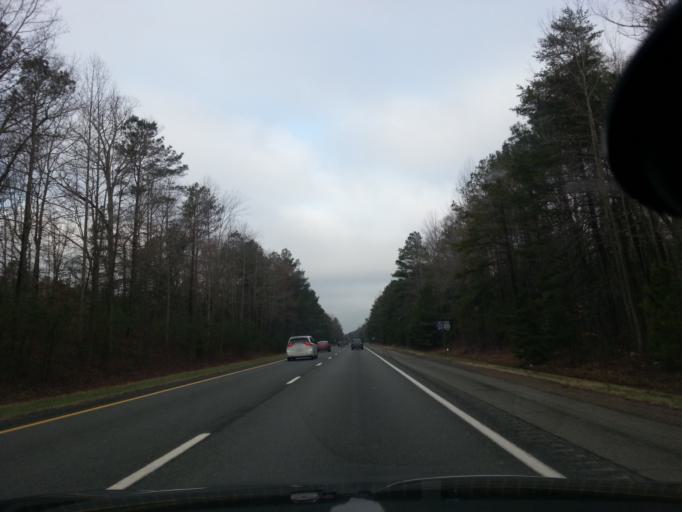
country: US
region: Virginia
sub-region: New Kent County
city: New Kent
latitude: 37.5063
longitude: -77.0949
